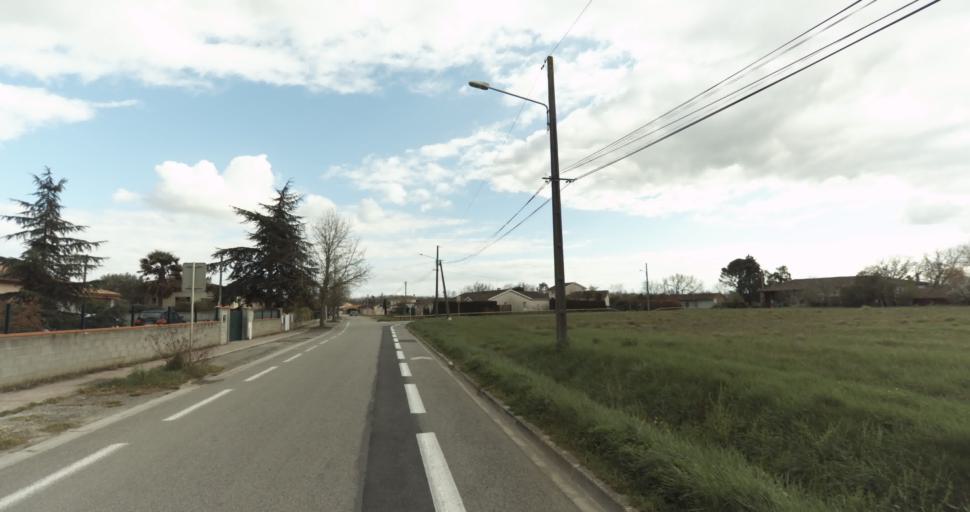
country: FR
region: Midi-Pyrenees
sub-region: Departement de la Haute-Garonne
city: Auterive
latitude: 43.3427
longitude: 1.4856
